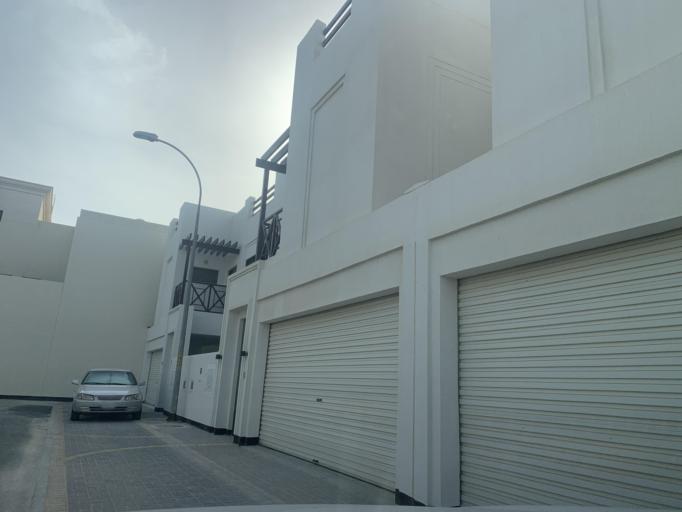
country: BH
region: Muharraq
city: Al Muharraq
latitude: 26.3180
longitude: 50.6263
